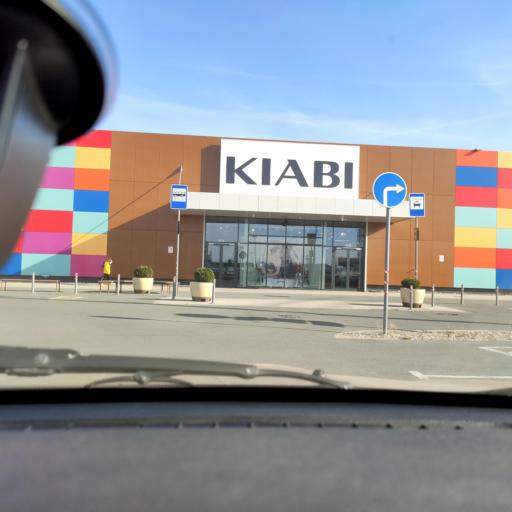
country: RU
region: Samara
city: Tol'yatti
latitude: 53.5496
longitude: 49.3436
